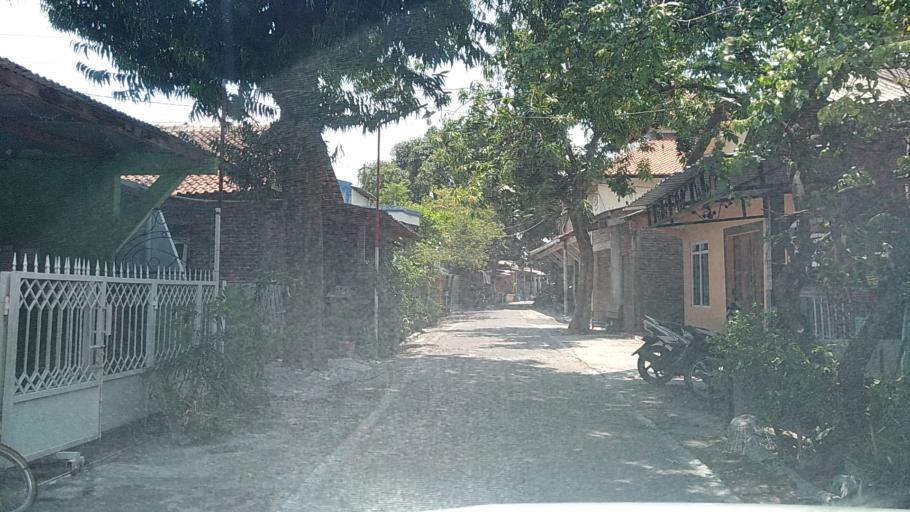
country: ID
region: Central Java
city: Semarang
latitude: -7.0038
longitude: 110.4477
